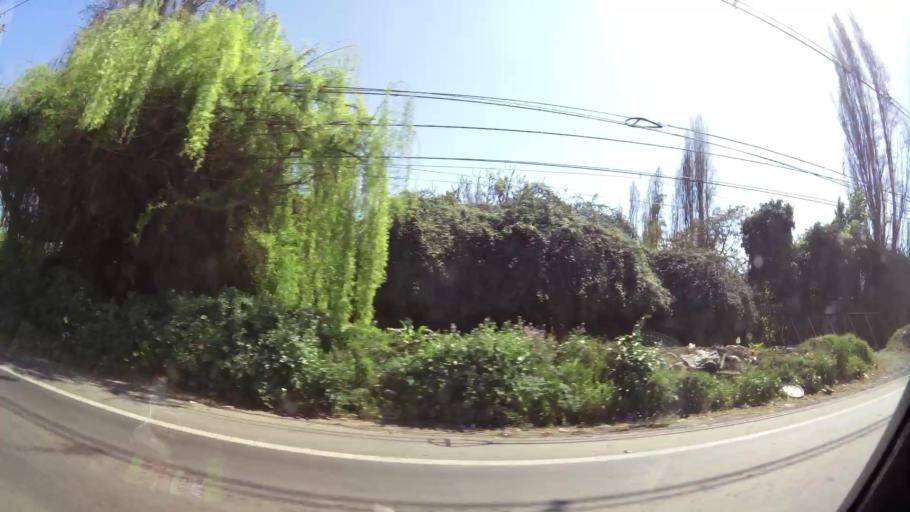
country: CL
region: Santiago Metropolitan
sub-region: Provincia de Talagante
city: Talagante
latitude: -33.6329
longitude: -70.9111
